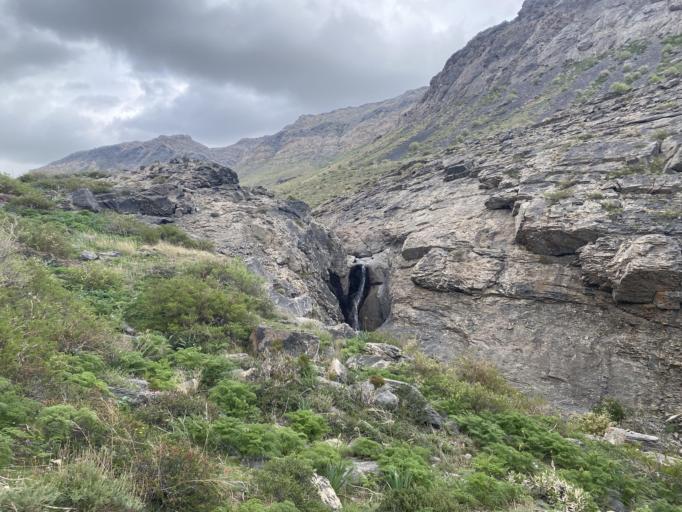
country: KZ
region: Ongtustik Qazaqstan
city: Ashchysay
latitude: 43.6419
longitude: 68.8919
